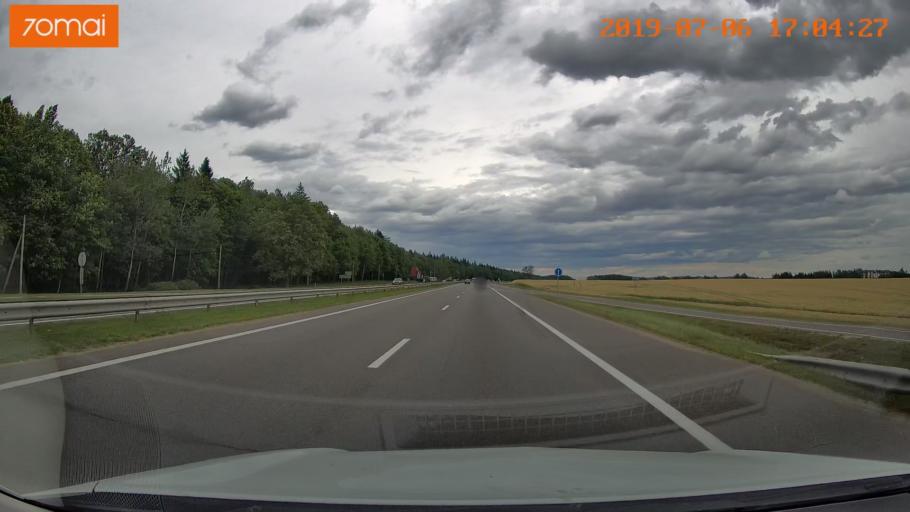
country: BY
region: Minsk
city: Khatsyezhyna
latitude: 53.9175
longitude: 27.2964
